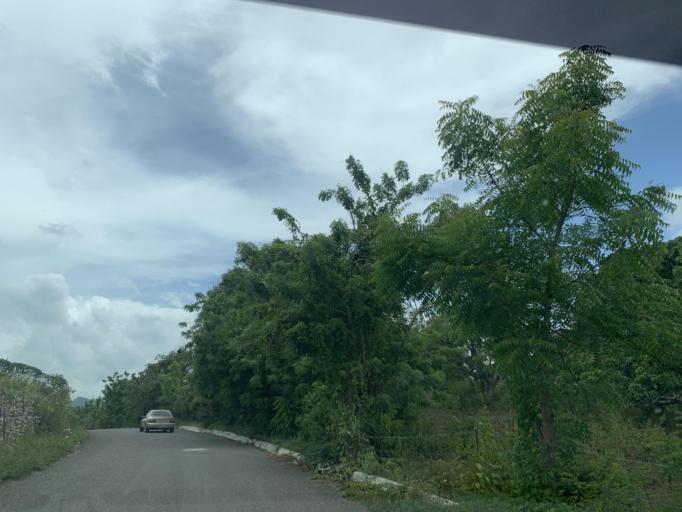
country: DO
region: Puerto Plata
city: Imbert
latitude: 19.8213
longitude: -70.7782
